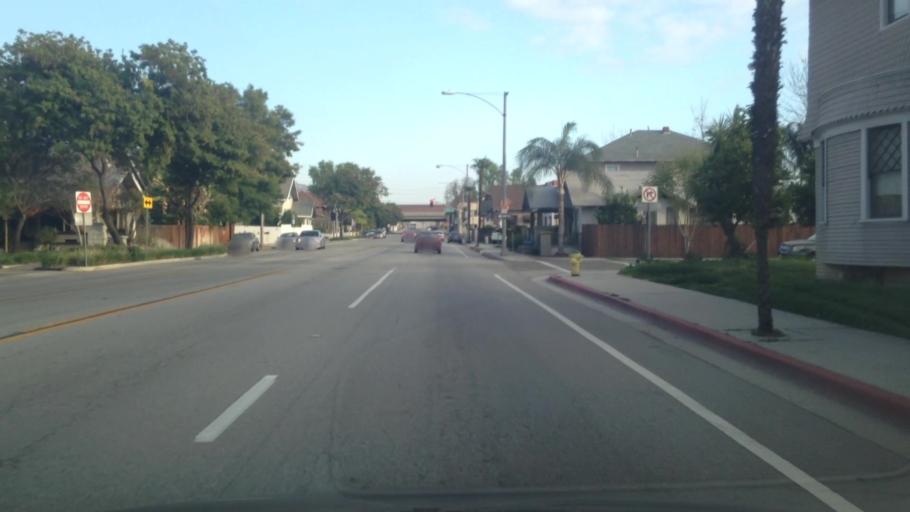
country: US
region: California
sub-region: Riverside County
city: Rubidoux
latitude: 33.9858
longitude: -117.3693
